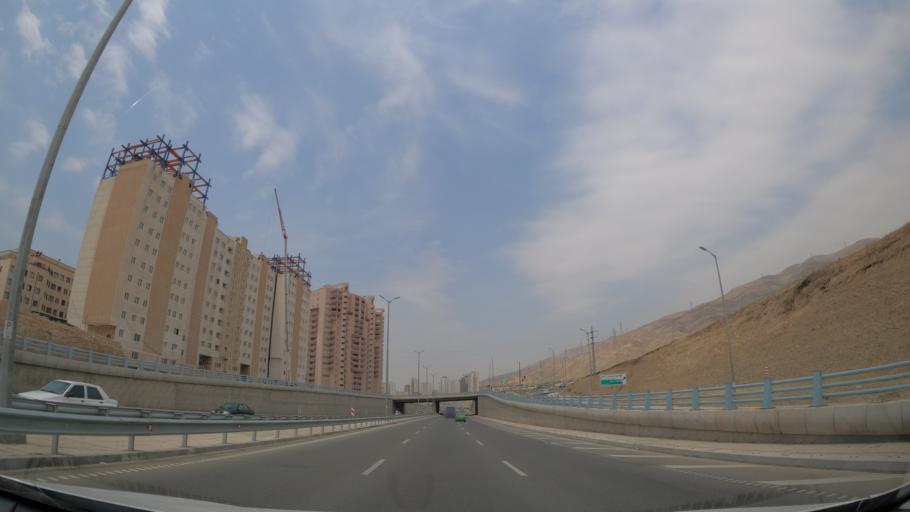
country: IR
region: Tehran
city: Shahr-e Qods
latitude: 35.7515
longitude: 51.1561
